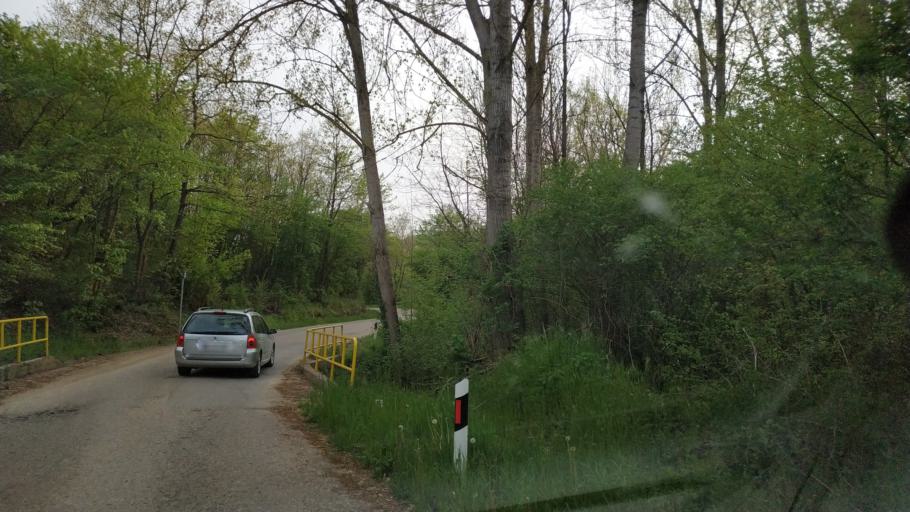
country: RS
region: Central Serbia
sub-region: Nisavski Okrug
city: Aleksinac
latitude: 43.4684
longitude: 21.8065
